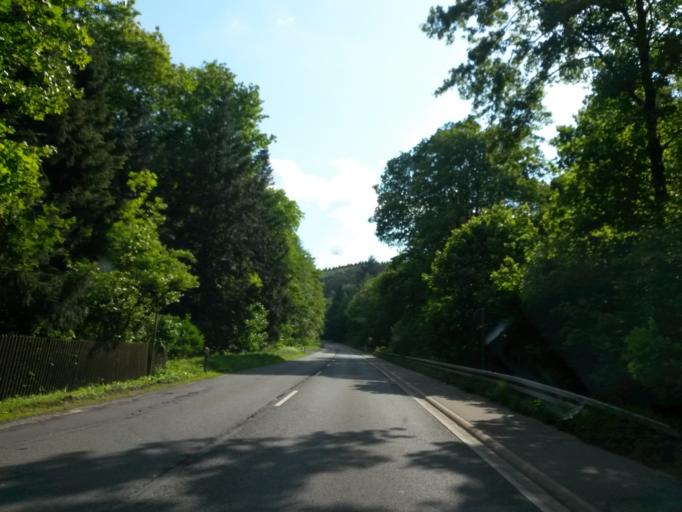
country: DE
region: North Rhine-Westphalia
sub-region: Regierungsbezirk Arnsberg
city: Herscheid
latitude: 51.1903
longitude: 7.7944
